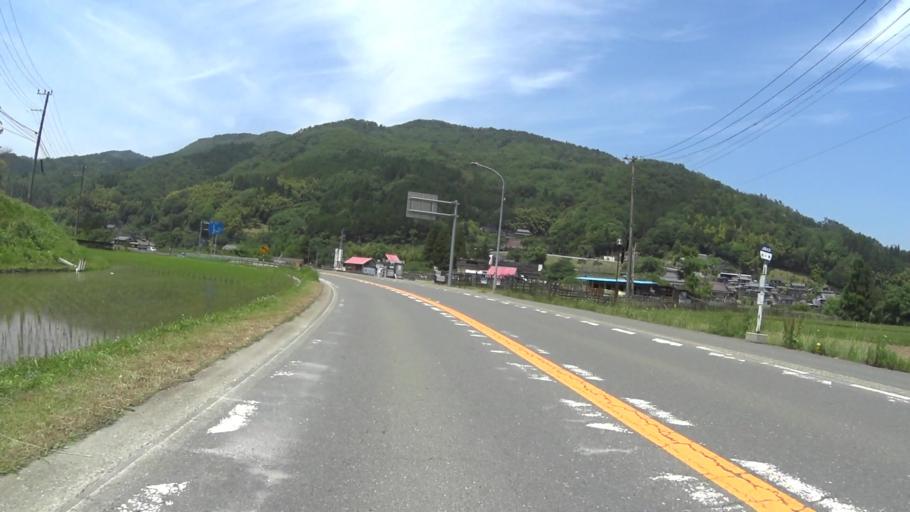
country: JP
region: Kyoto
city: Ayabe
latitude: 35.2070
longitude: 135.2846
